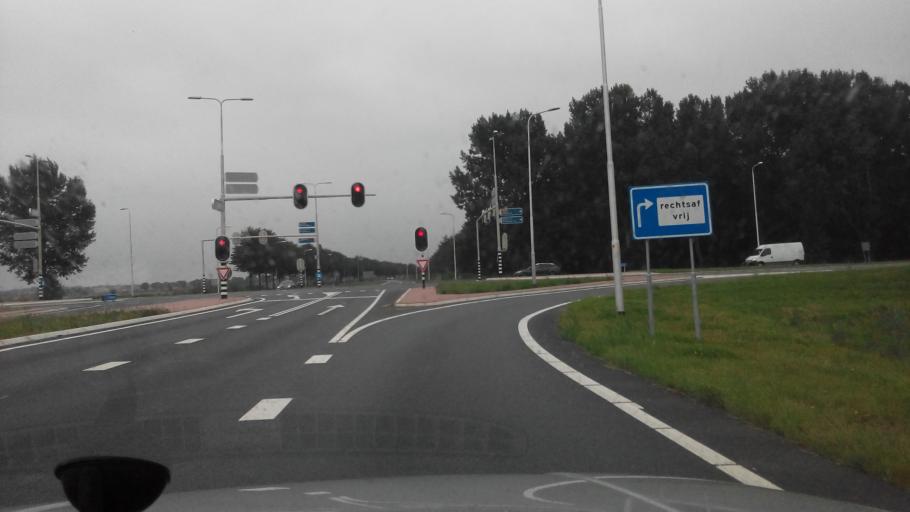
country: NL
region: Flevoland
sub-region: Gemeente Zeewolde
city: Zeewolde
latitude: 52.3484
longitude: 5.5009
